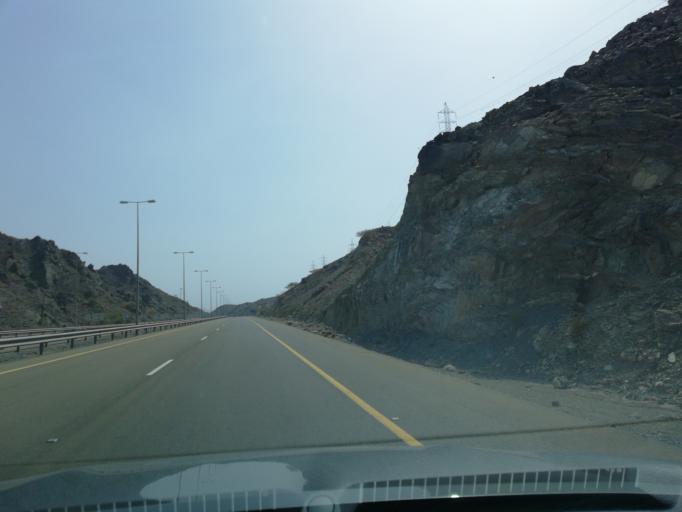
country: OM
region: Al Batinah
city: Al Liwa'
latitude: 24.2372
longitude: 56.3460
